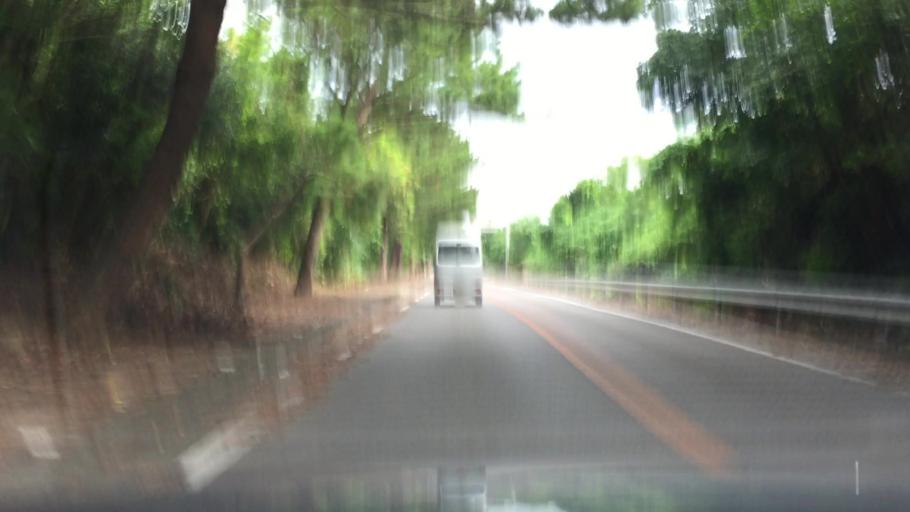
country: JP
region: Okinawa
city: Ishigaki
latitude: 24.4080
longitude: 124.1449
